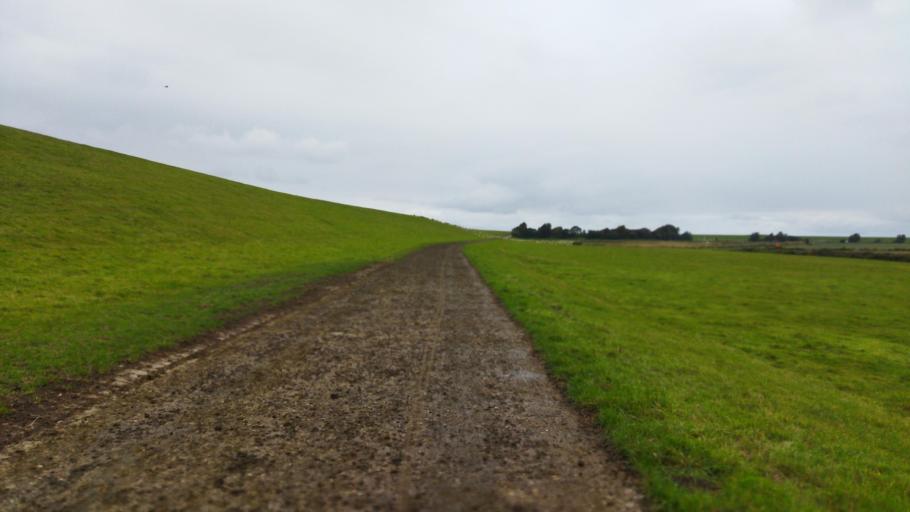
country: DE
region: Lower Saxony
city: Hinte
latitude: 53.4779
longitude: 7.0307
